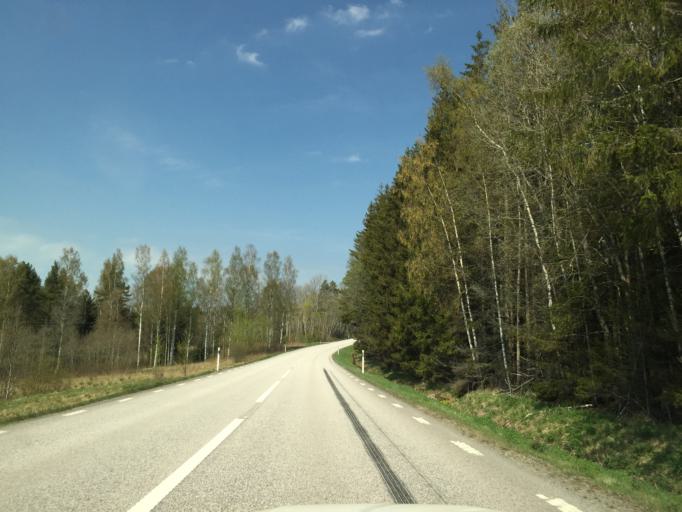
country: SE
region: Vaestra Goetaland
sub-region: Bengtsfors Kommun
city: Dals Langed
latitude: 58.9019
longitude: 12.2186
